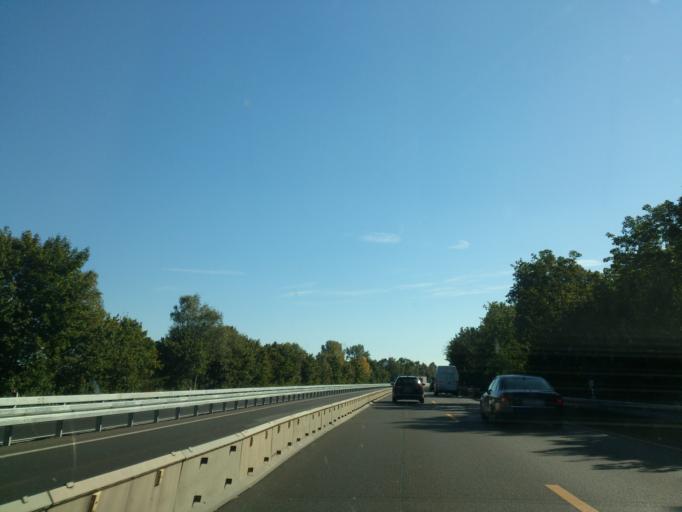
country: DE
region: North Rhine-Westphalia
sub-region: Regierungsbezirk Detmold
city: Hovelhof
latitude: 51.8297
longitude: 8.6960
